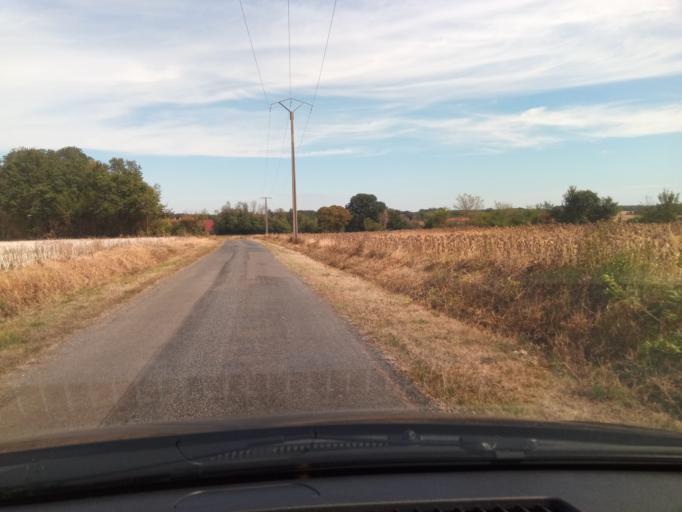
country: FR
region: Poitou-Charentes
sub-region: Departement de la Vienne
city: Chauvigny
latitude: 46.5547
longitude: 0.7412
